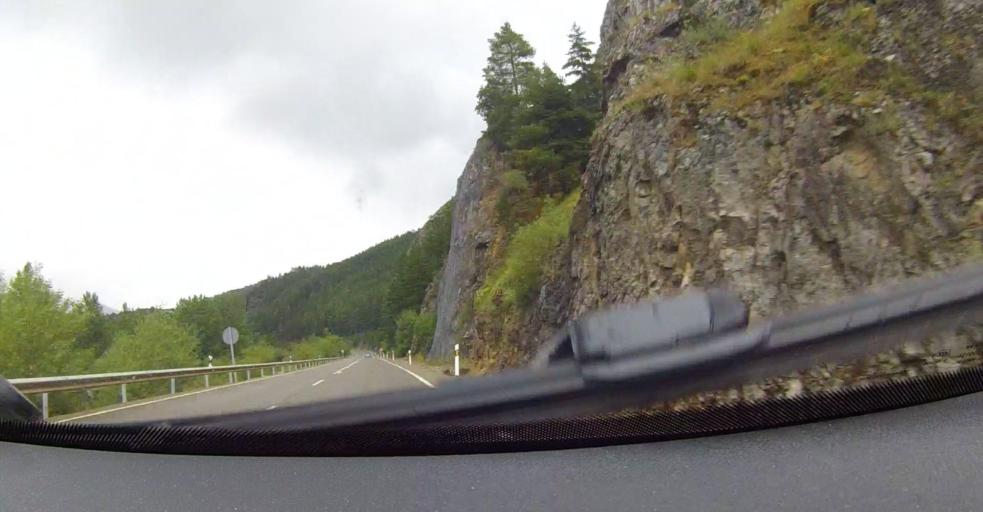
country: ES
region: Castille and Leon
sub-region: Provincia de Leon
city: Cistierna
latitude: 42.8207
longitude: -5.1229
